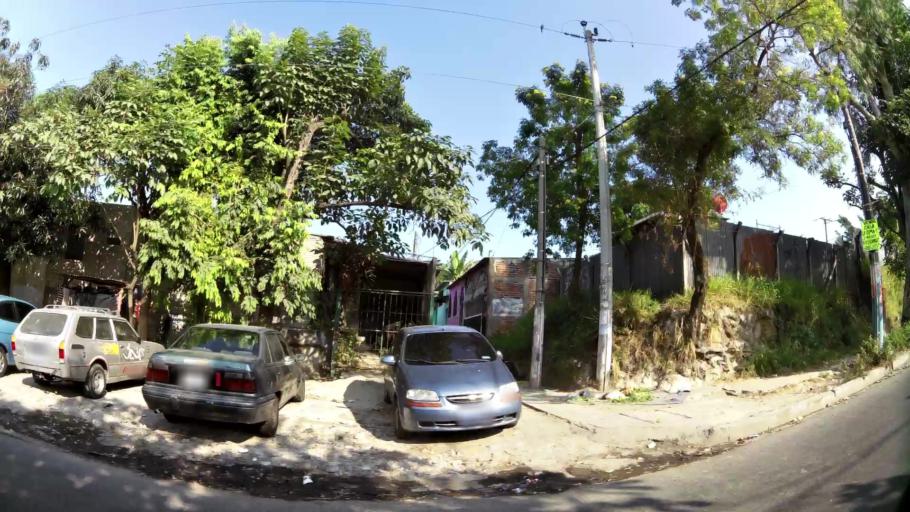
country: SV
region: San Salvador
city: Ilopango
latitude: 13.7164
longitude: -89.1056
